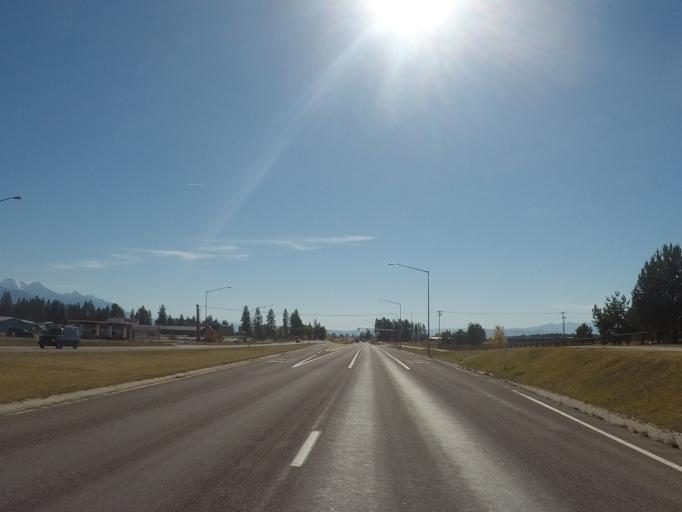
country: US
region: Montana
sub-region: Lake County
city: Pablo
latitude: 47.5965
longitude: -114.1132
